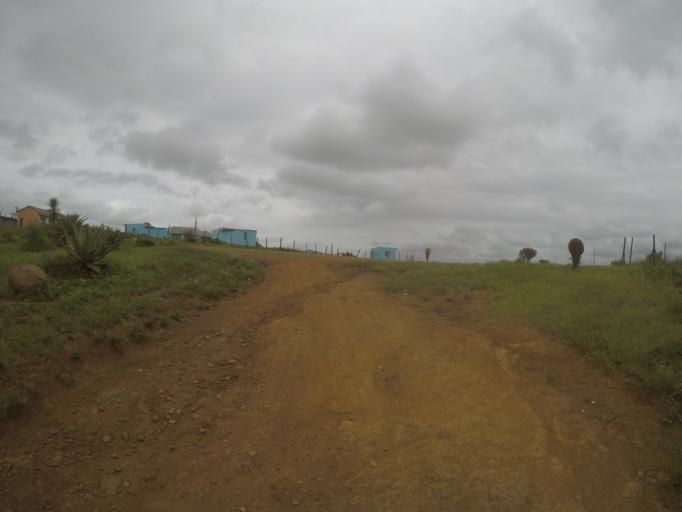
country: ZA
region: KwaZulu-Natal
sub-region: uThungulu District Municipality
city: Empangeni
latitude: -28.6033
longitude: 31.8452
